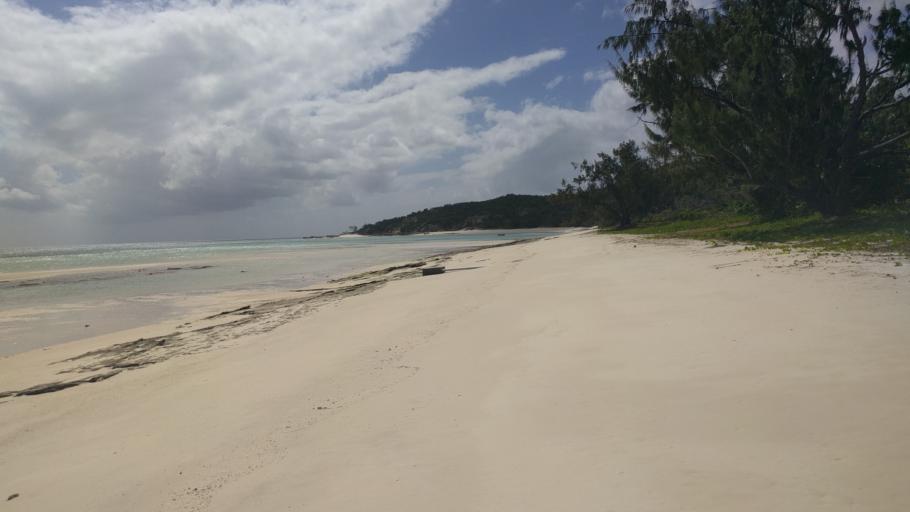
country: AU
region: Queensland
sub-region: Cook
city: Cooktown
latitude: -14.6789
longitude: 145.4474
